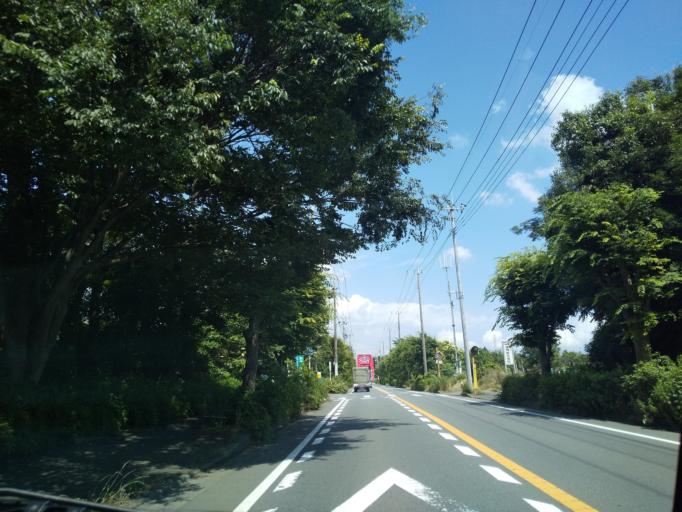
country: JP
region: Kanagawa
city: Zama
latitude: 35.4900
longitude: 139.4184
